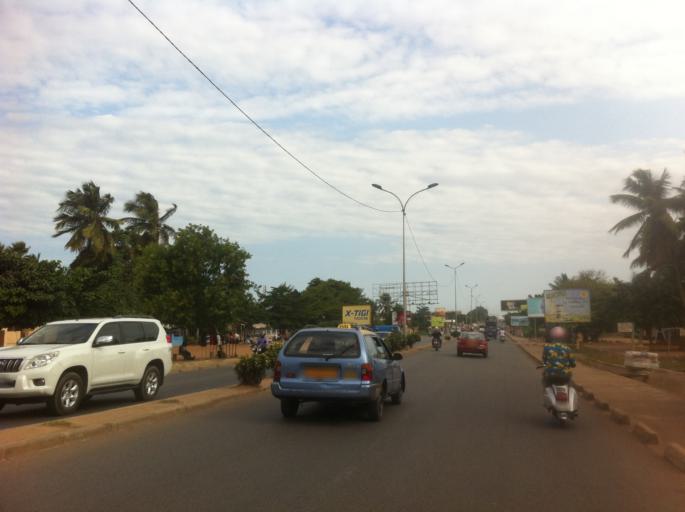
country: TG
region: Maritime
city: Lome
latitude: 6.1627
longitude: 1.2019
